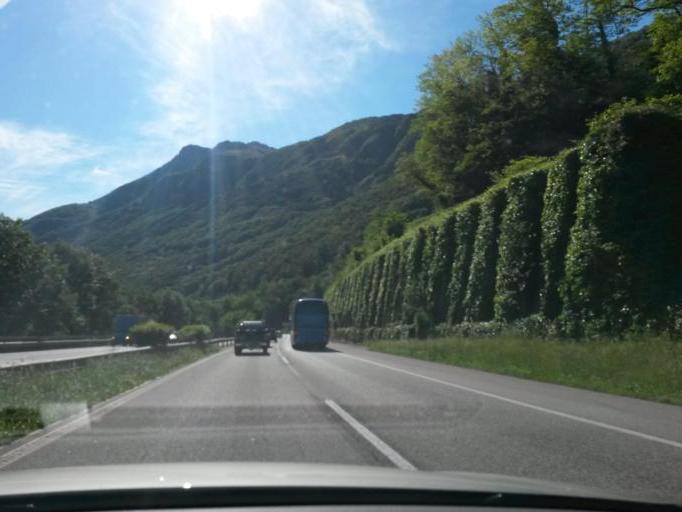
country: CH
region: Ticino
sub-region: Bellinzona District
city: Cadenazzo
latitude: 46.1509
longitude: 8.9698
